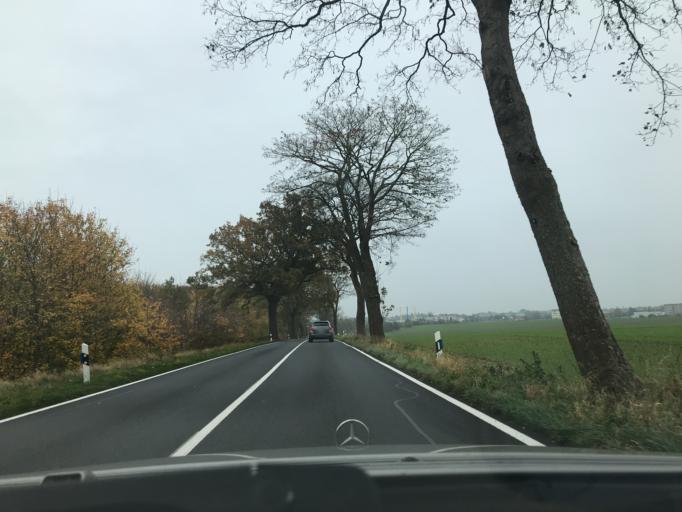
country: DE
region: Mecklenburg-Vorpommern
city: Wolgast
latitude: 54.0661
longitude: 13.7608
